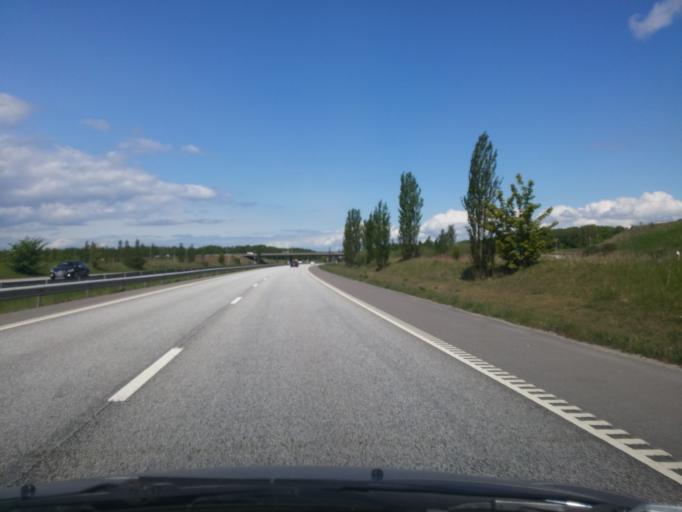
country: SE
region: Skane
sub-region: Malmo
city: Tygelsjo
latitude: 55.5516
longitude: 13.0006
